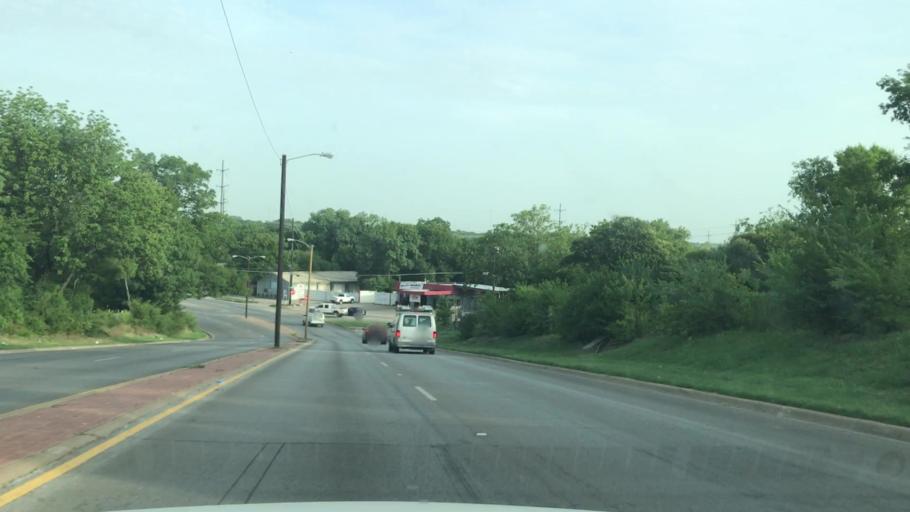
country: US
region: Texas
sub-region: Dallas County
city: Dallas
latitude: 32.7825
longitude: -96.7254
